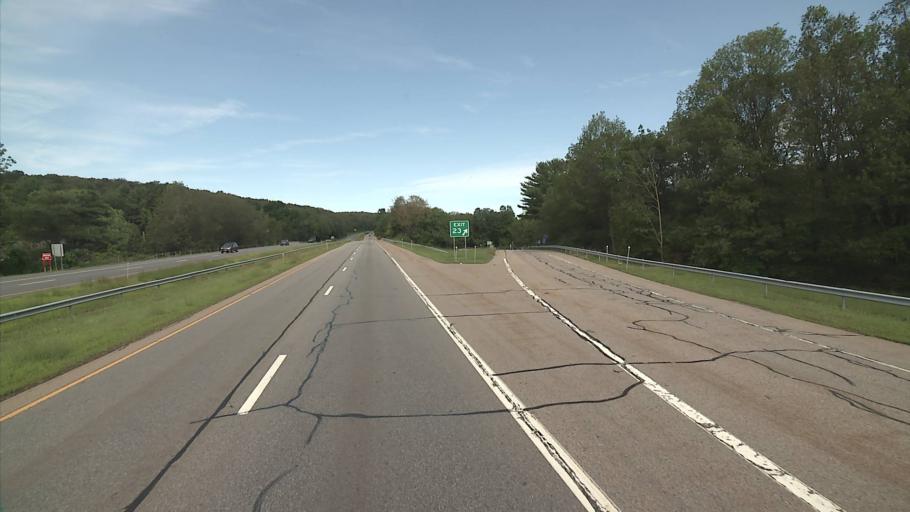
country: US
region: Connecticut
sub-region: New London County
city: Montville Center
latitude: 41.5617
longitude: -72.1626
